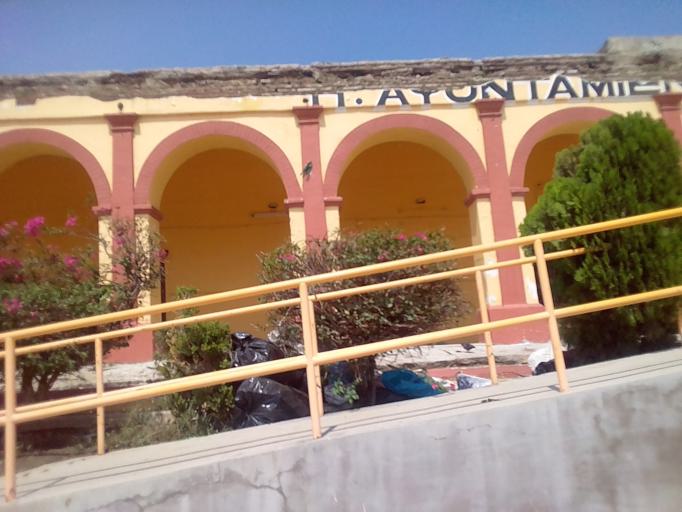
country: MX
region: Oaxaca
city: Union Hidalgo
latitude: 16.4729
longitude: -94.8291
